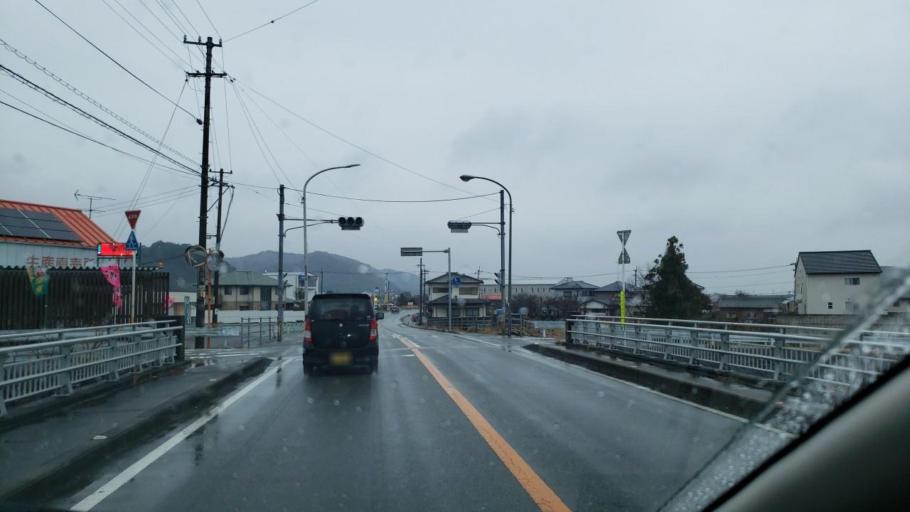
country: JP
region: Tokushima
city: Narutocho-mitsuishi
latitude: 34.1649
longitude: 134.5706
